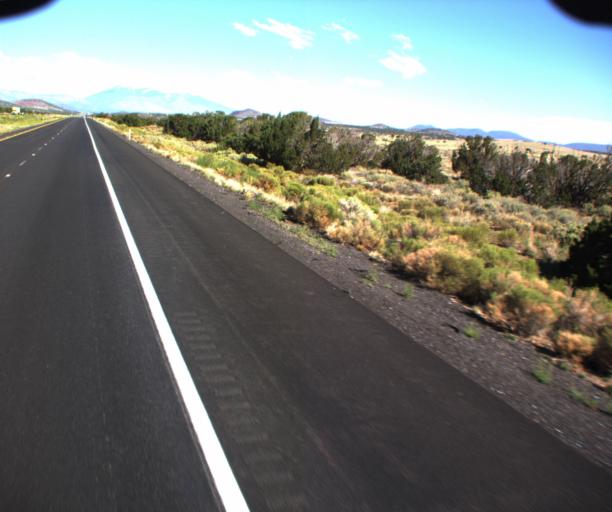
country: US
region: Arizona
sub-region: Coconino County
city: Flagstaff
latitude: 35.1793
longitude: -111.3506
